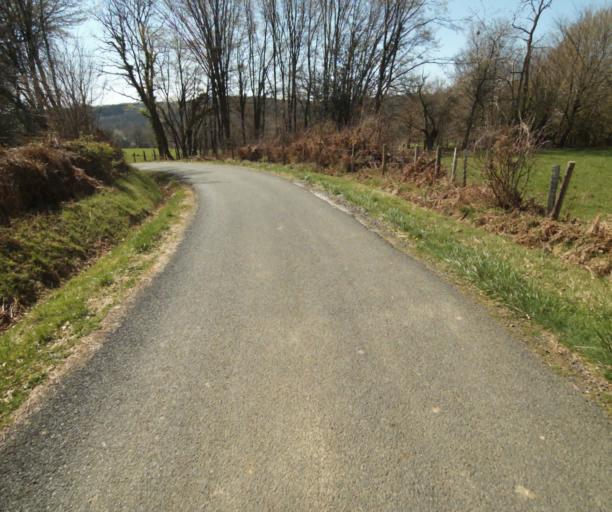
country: FR
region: Limousin
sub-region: Departement de la Correze
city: Saint-Clement
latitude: 45.3252
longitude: 1.6930
